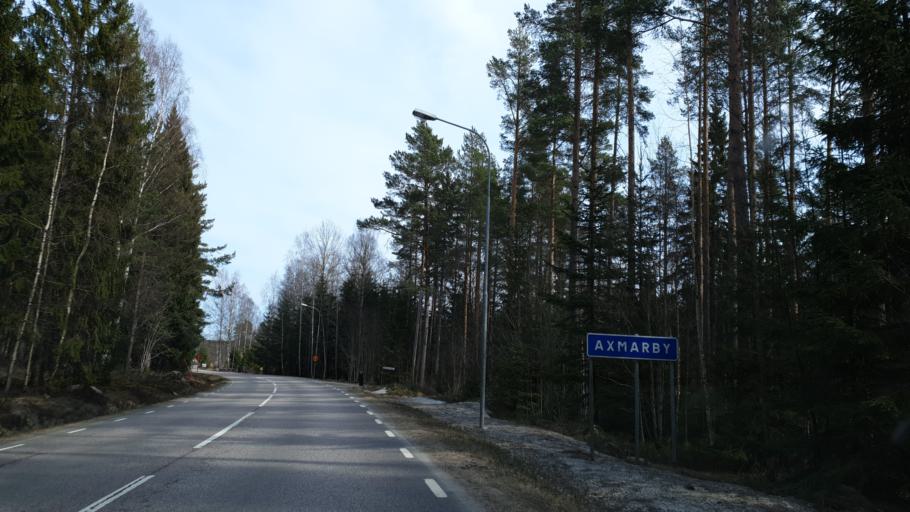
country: SE
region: Gaevleborg
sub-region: Gavle Kommun
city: Norrsundet
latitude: 60.9993
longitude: 17.1066
